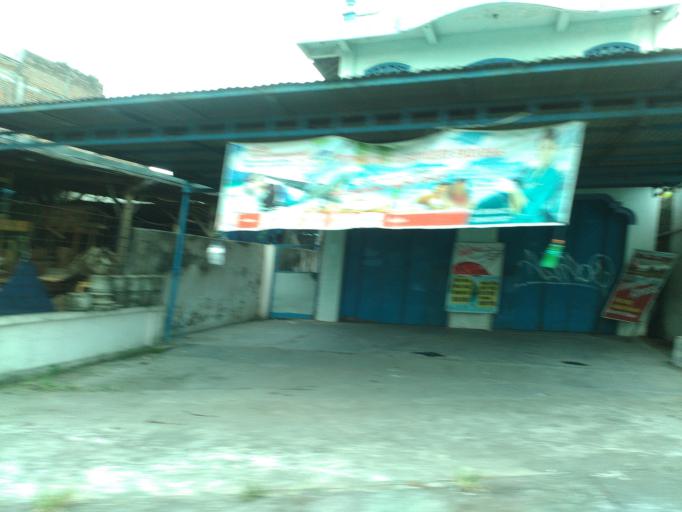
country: ID
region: Central Java
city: Ceper
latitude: -7.6599
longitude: 110.6744
